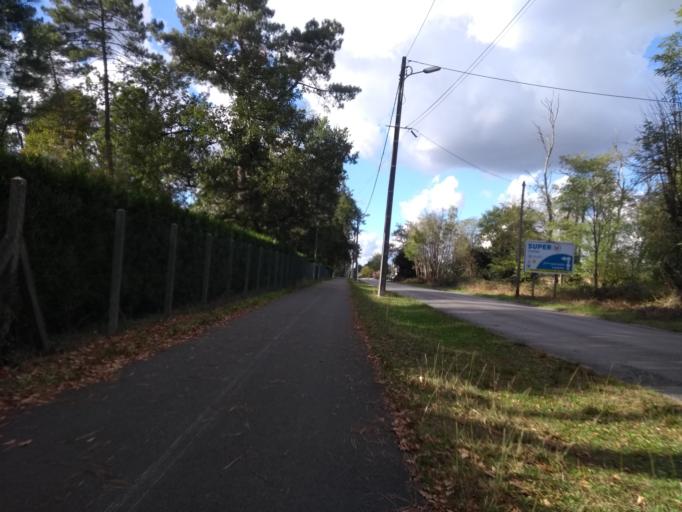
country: FR
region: Aquitaine
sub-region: Departement de la Gironde
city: Cestas
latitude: 44.7357
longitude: -0.6720
